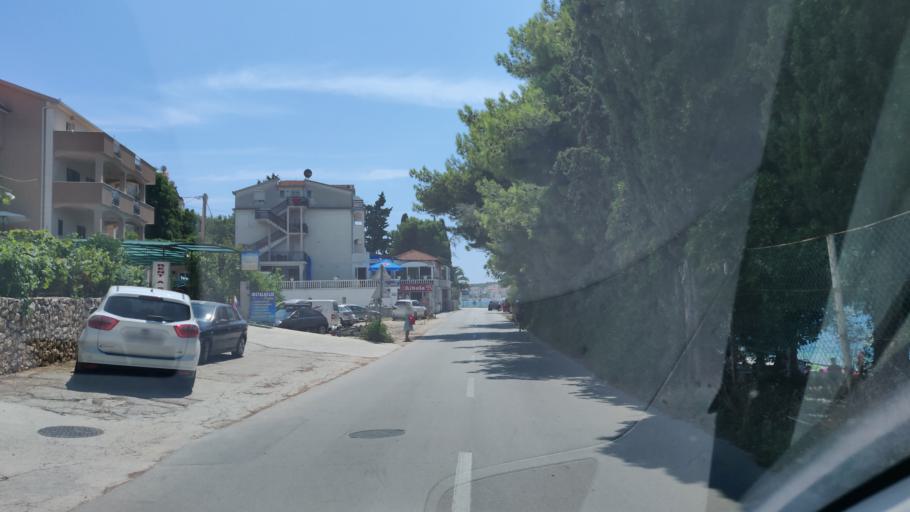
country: HR
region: Splitsko-Dalmatinska
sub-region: Grad Trogir
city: Trogir
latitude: 43.5048
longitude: 16.2582
